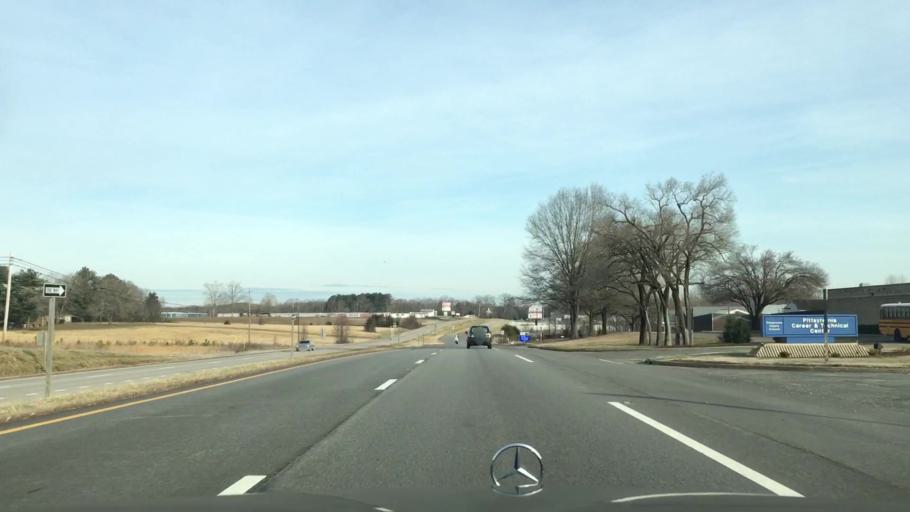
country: US
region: Virginia
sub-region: Pittsylvania County
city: Chatham
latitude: 36.7643
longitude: -79.3890
